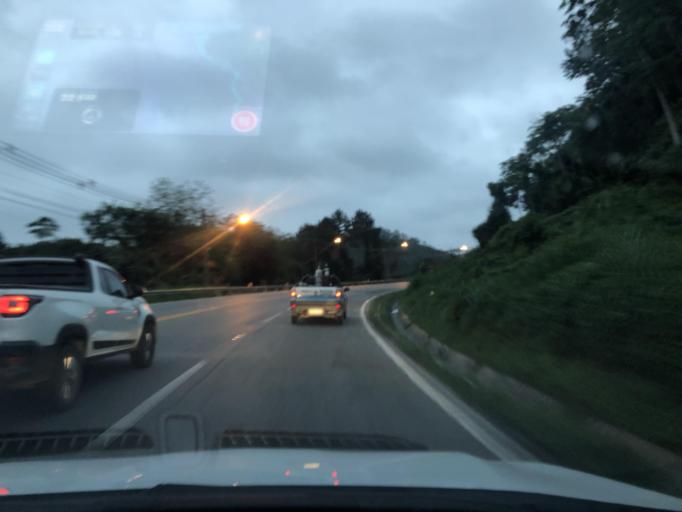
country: BR
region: Santa Catarina
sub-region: Pomerode
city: Pomerode
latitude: -26.7527
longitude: -49.0712
